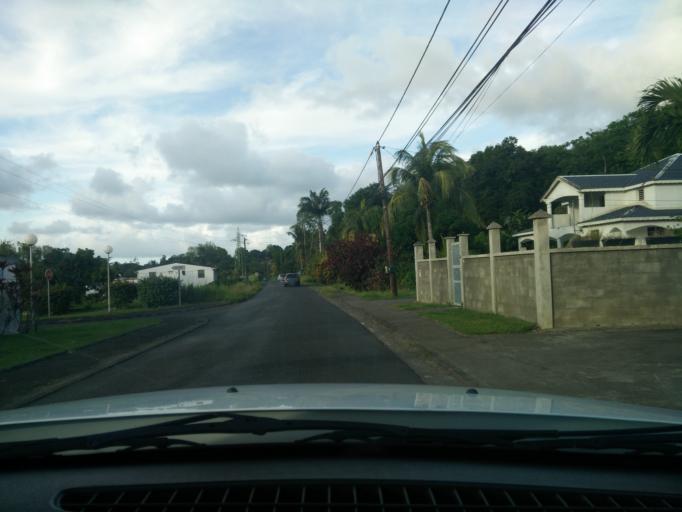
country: GP
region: Guadeloupe
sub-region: Guadeloupe
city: Les Abymes
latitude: 16.2525
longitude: -61.5075
